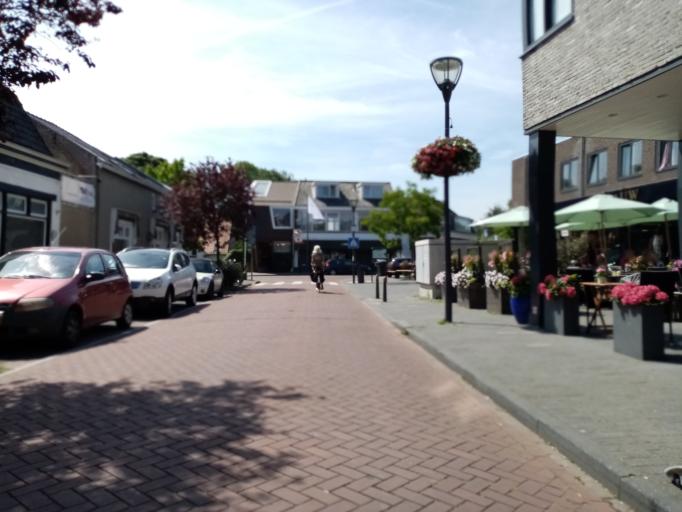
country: NL
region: South Holland
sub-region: Gemeente Oegstgeest
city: Oegstgeest
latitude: 52.1781
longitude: 4.4702
